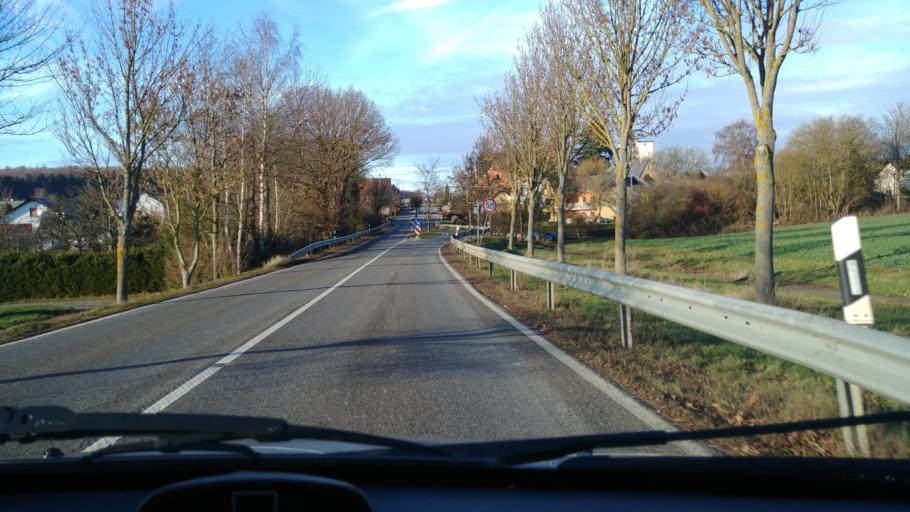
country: DE
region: Rheinland-Pfalz
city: Pohl
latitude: 50.2488
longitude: 7.8681
